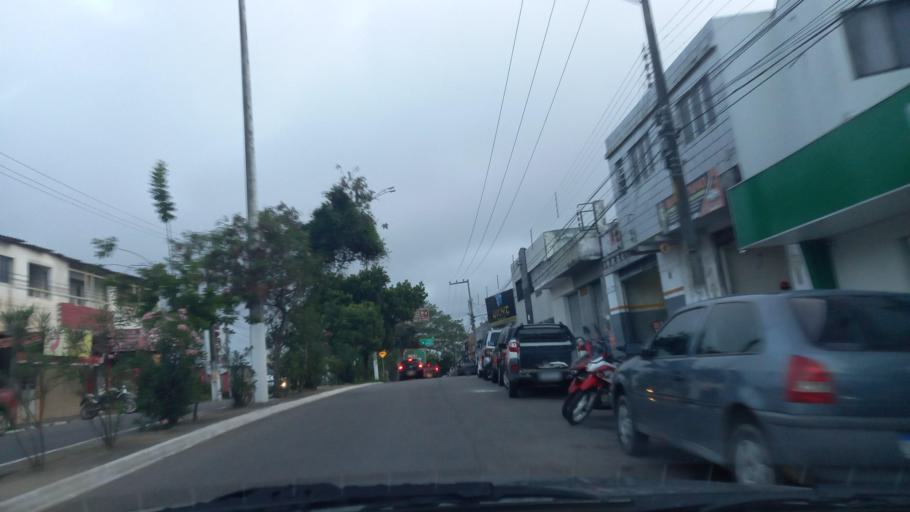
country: BR
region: Pernambuco
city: Garanhuns
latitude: -8.8787
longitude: -36.4759
